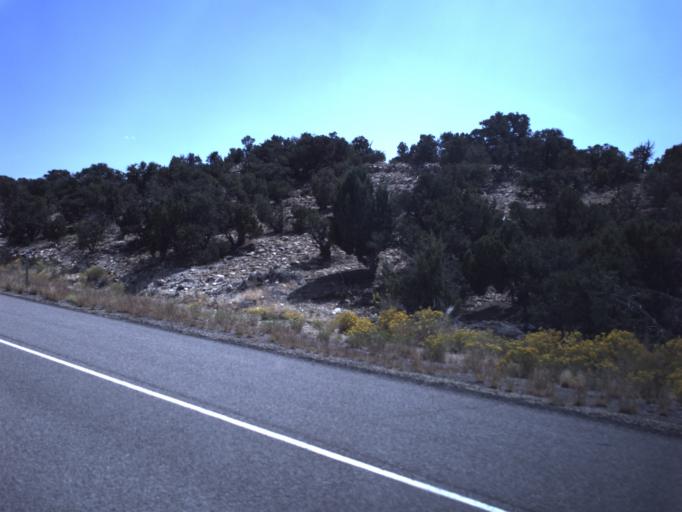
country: US
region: Utah
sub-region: Emery County
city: Ferron
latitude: 38.8521
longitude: -110.9075
